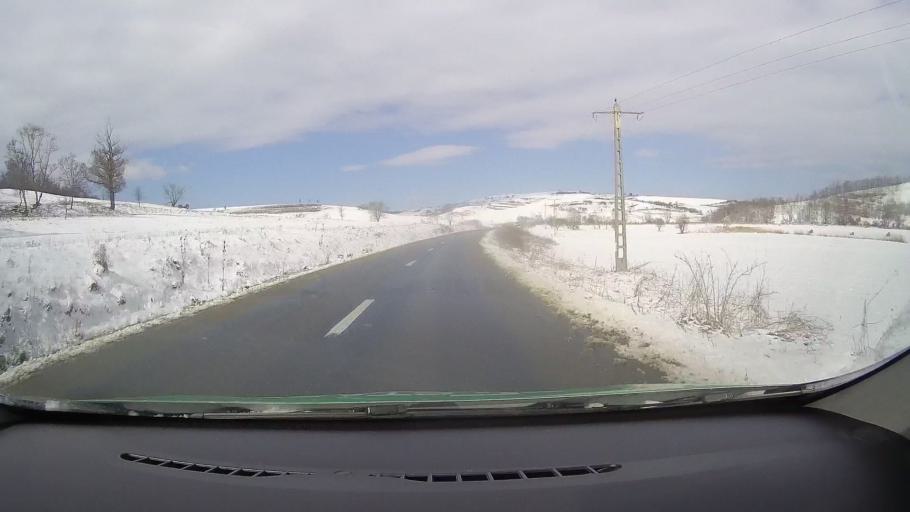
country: RO
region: Sibiu
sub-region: Comuna Altina
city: Altina
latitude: 45.9713
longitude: 24.4668
